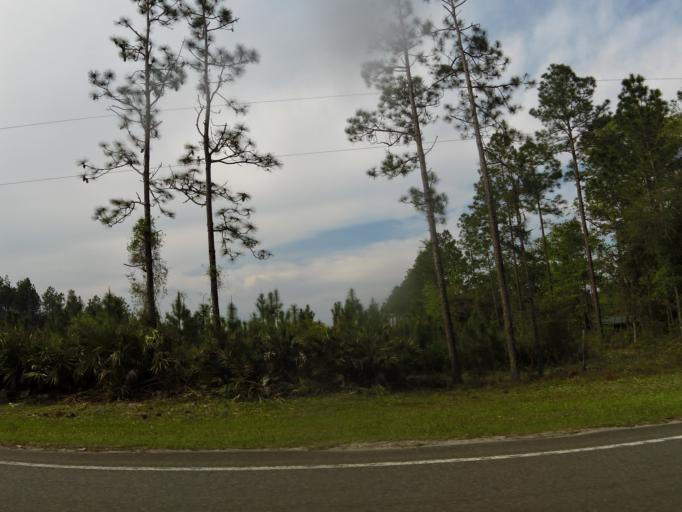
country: US
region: Georgia
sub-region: Camden County
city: Kingsland
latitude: 30.6961
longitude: -81.7253
